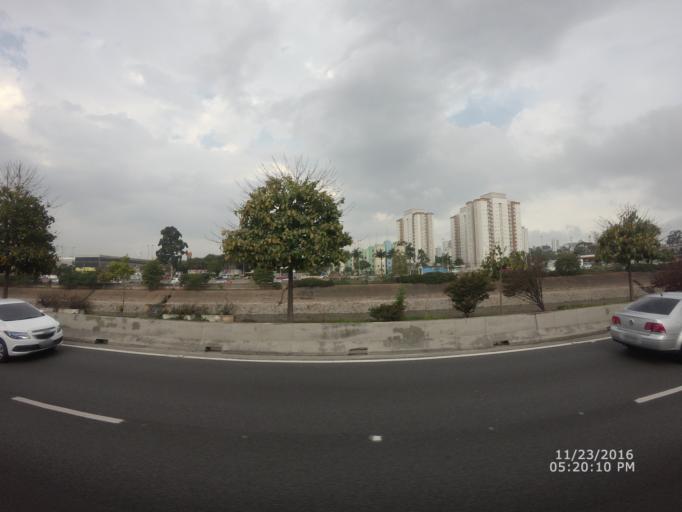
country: BR
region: Sao Paulo
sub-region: Guarulhos
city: Guarulhos
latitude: -23.5195
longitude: -46.5564
